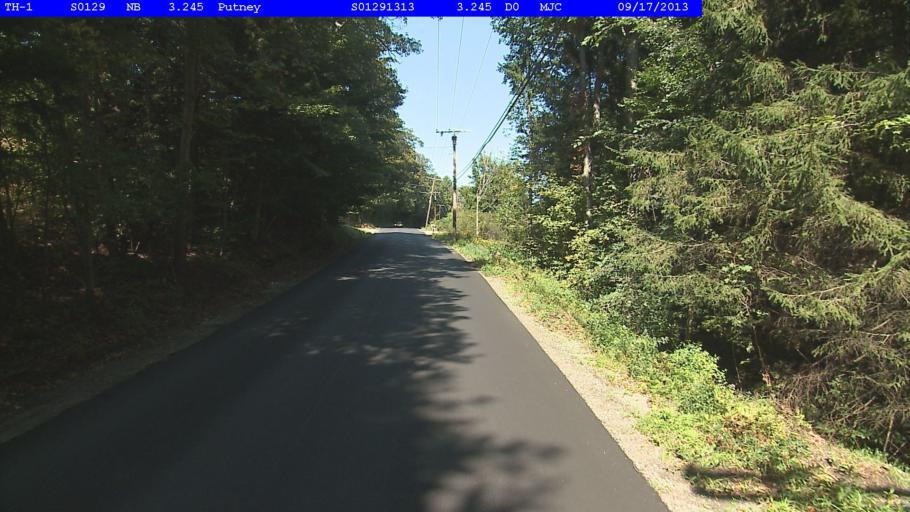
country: US
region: New Hampshire
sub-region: Cheshire County
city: Westmoreland
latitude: 43.0185
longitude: -72.5259
